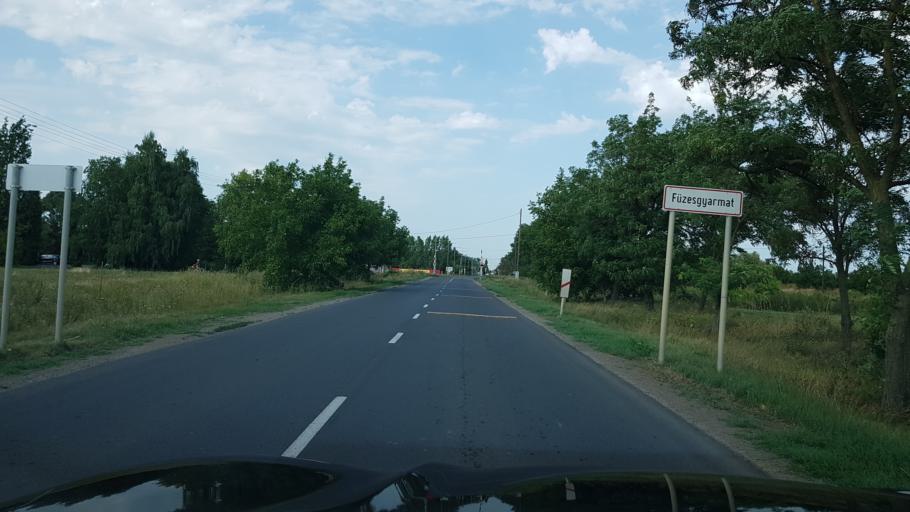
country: HU
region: Bekes
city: Fuzesgyarmat
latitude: 47.0893
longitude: 21.2016
